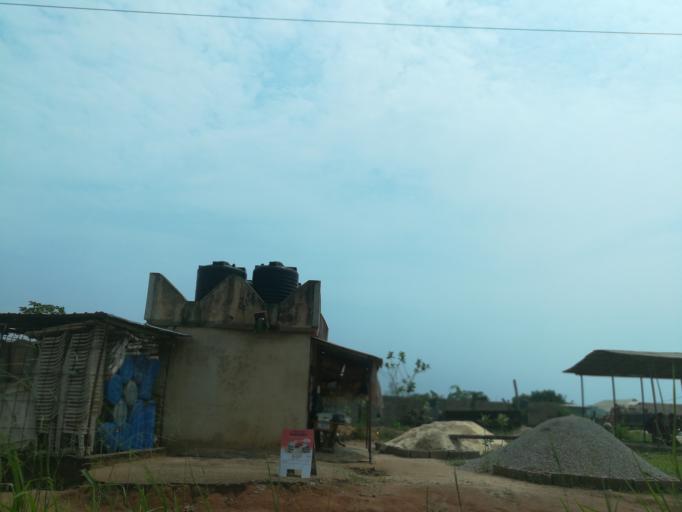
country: NG
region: Lagos
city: Ikorodu
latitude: 6.6032
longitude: 3.6095
